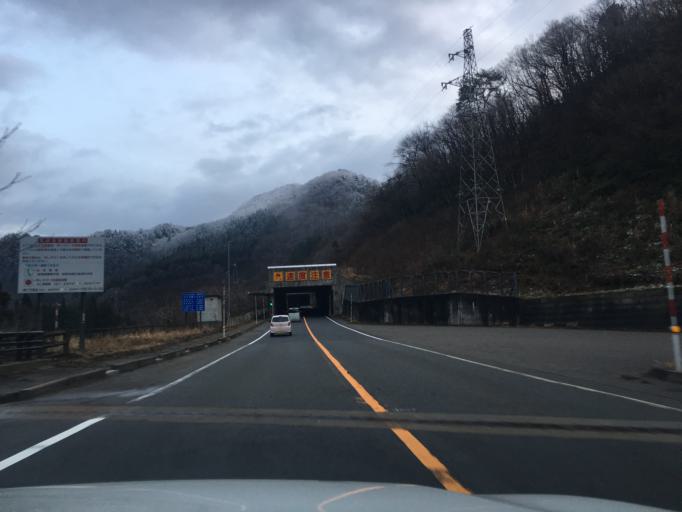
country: JP
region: Niigata
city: Murakami
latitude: 38.4014
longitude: 139.5568
